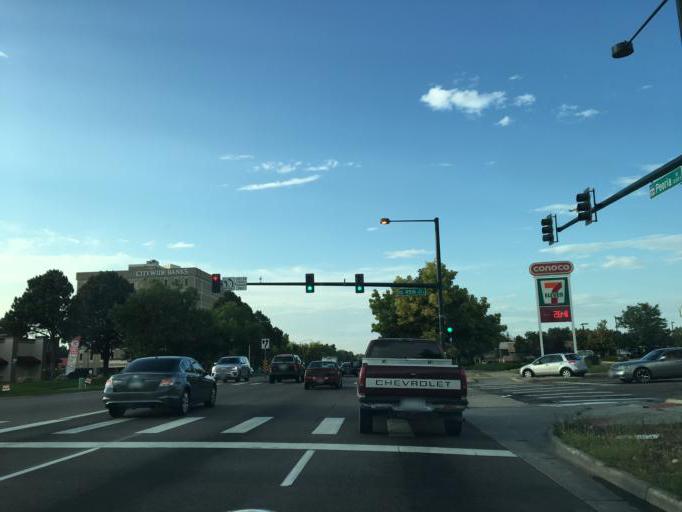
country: US
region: Colorado
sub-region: Adams County
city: Aurora
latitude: 39.7778
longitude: -104.8469
